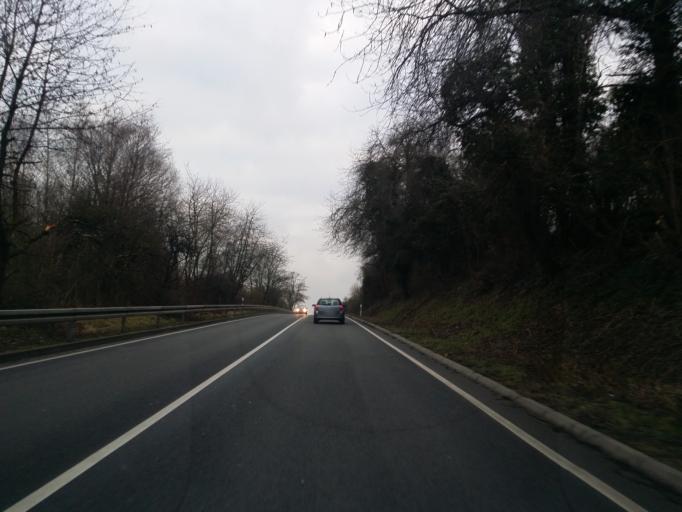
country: DE
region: Hesse
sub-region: Regierungsbezirk Darmstadt
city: Wiesbaden
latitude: 50.1059
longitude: 8.2784
